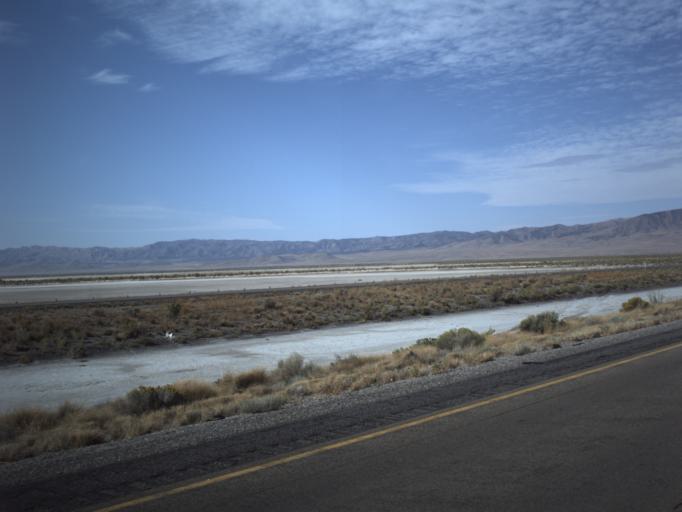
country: US
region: Utah
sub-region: Tooele County
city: Grantsville
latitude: 40.7532
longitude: -112.7240
